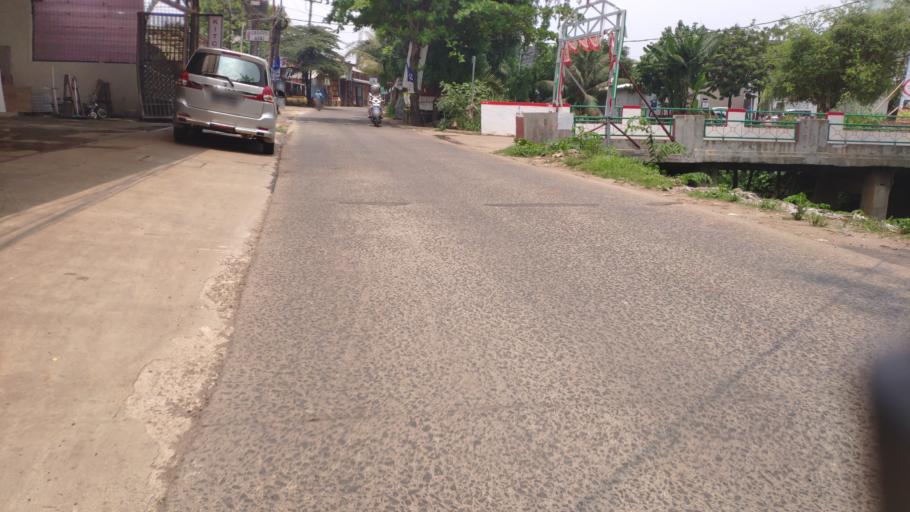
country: ID
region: West Java
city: Sawangan
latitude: -6.3737
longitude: 106.7900
